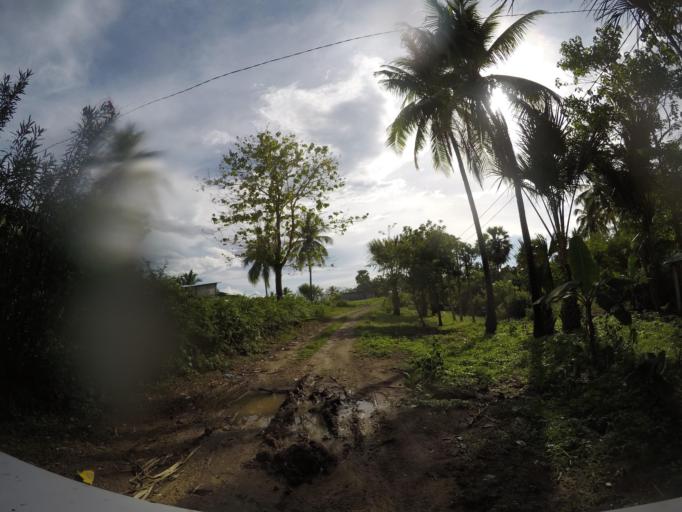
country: TL
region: Baucau
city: Baucau
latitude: -8.5041
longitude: 126.4501
